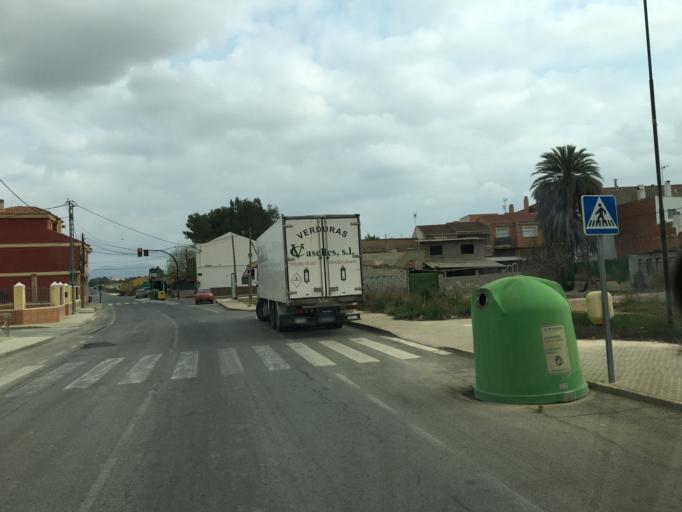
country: ES
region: Murcia
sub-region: Murcia
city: Beniel
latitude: 38.0275
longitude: -0.9803
